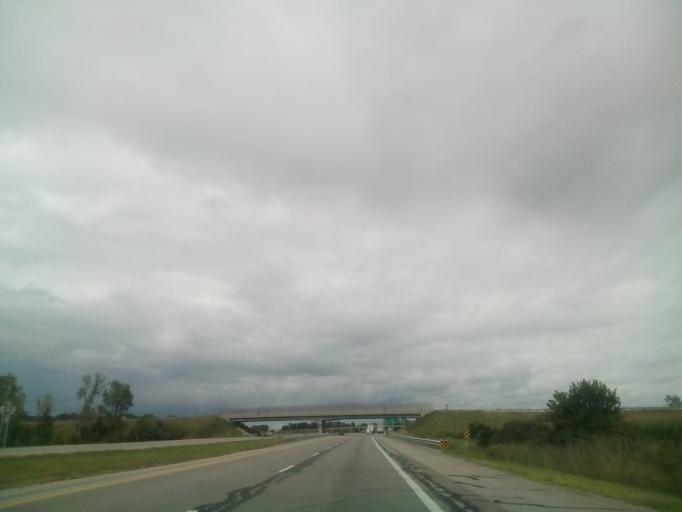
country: US
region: Ohio
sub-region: Fulton County
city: Burlington
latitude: 41.5901
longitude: -84.3287
